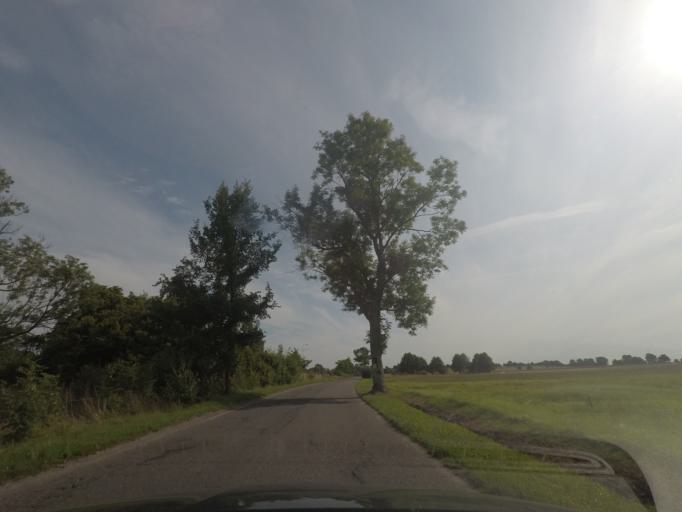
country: PL
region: Pomeranian Voivodeship
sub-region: Powiat slupski
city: Smoldzino
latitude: 54.6258
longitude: 17.2422
